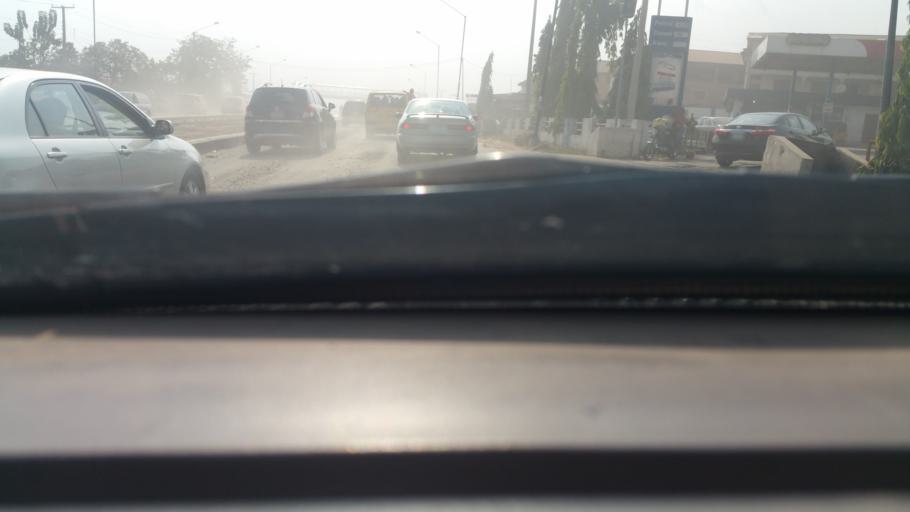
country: NG
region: Lagos
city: Agege
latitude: 6.6077
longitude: 3.3199
